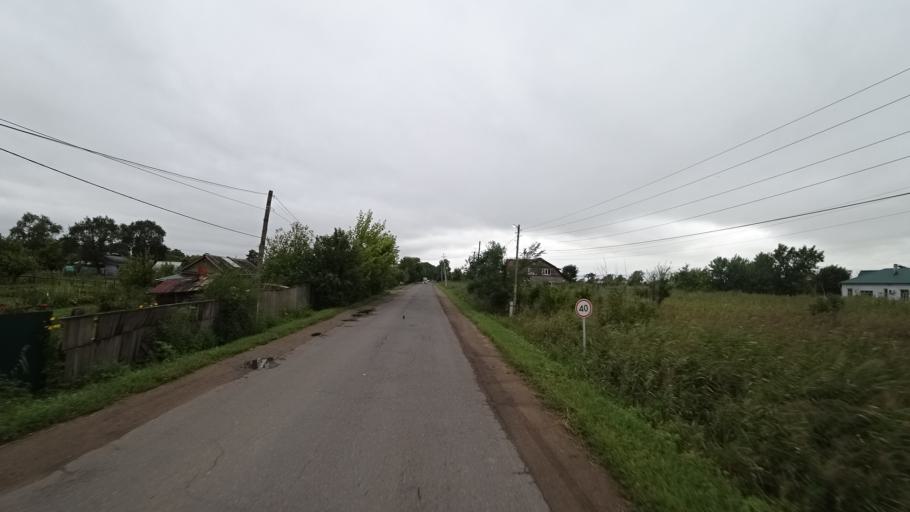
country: RU
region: Primorskiy
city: Chernigovka
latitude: 44.3386
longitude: 132.5347
